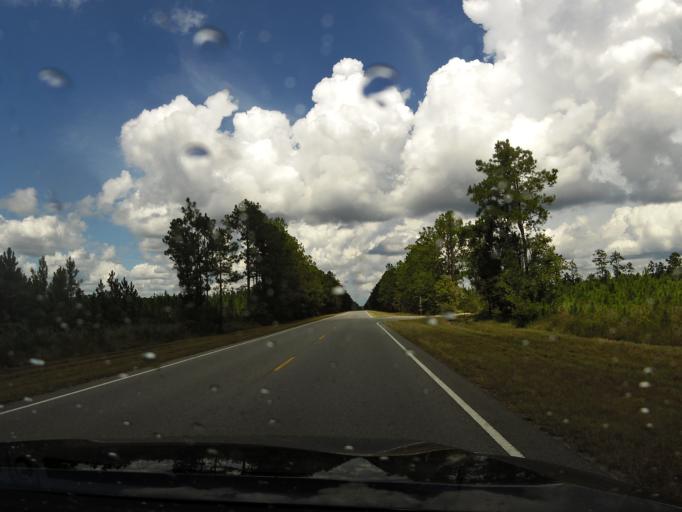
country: US
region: Georgia
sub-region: Charlton County
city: Folkston
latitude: 30.9033
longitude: -82.0177
